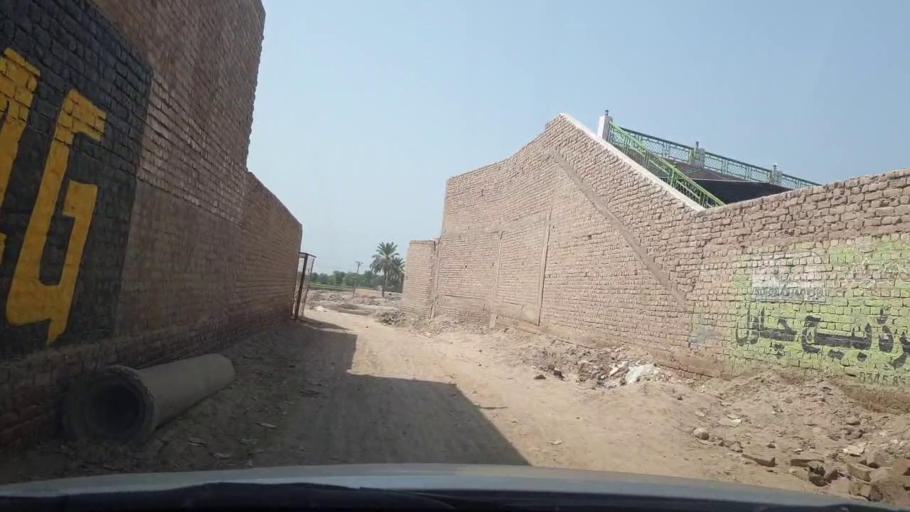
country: PK
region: Sindh
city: Rustam jo Goth
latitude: 28.0022
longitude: 68.7227
